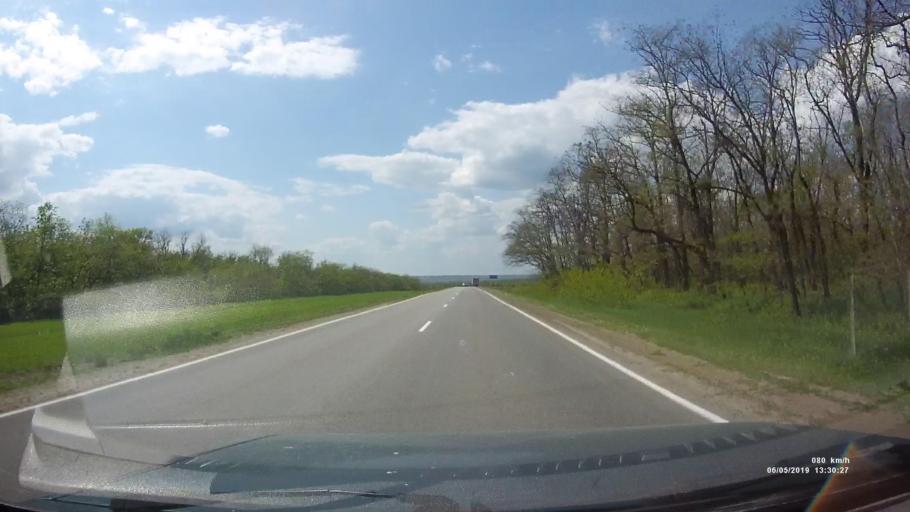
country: RU
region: Rostov
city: Ust'-Donetskiy
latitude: 47.6710
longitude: 40.8263
